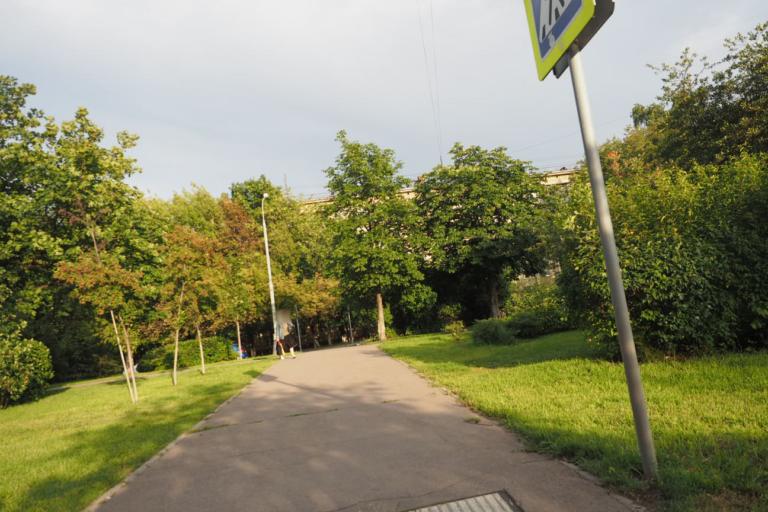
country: RU
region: Moscow
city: Novyye Cheremushki
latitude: 55.6801
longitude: 37.5765
